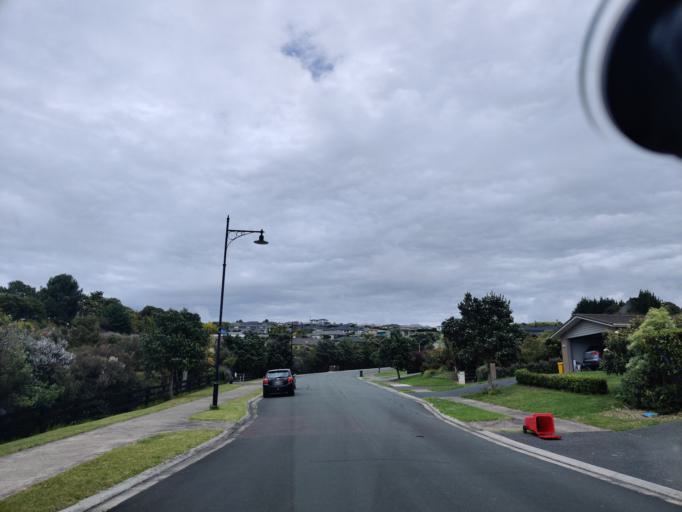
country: NZ
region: Auckland
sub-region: Auckland
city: Rothesay Bay
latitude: -36.5667
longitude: 174.6883
